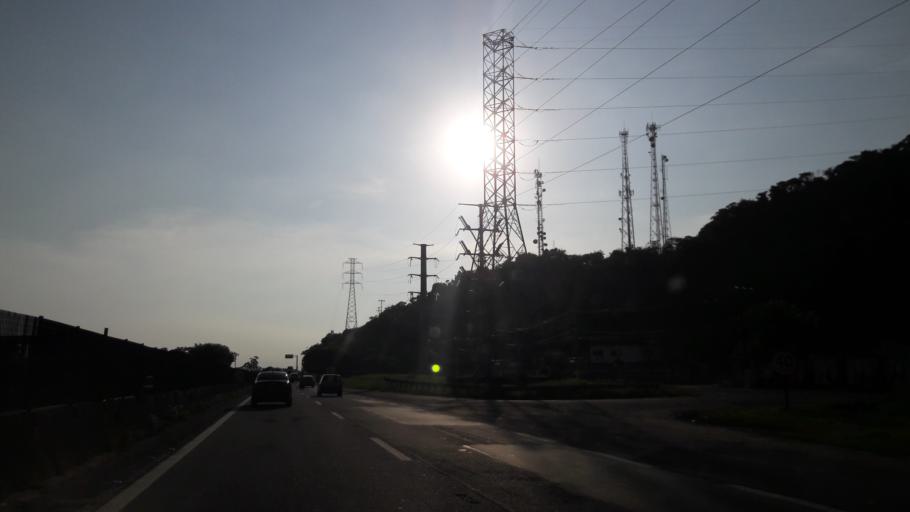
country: BR
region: Sao Paulo
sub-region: Mongagua
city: Mongagua
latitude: -24.0976
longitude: -46.6302
